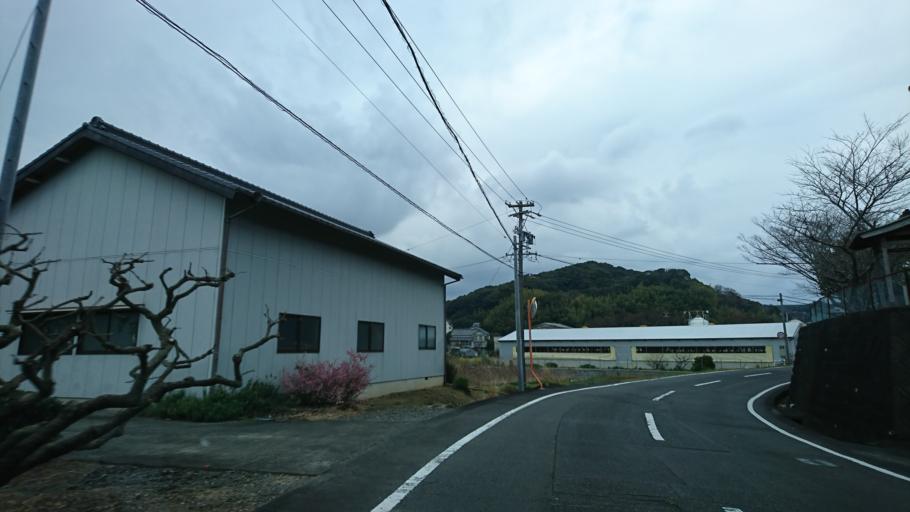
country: JP
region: Shizuoka
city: Sagara
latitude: 34.7321
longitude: 138.1815
